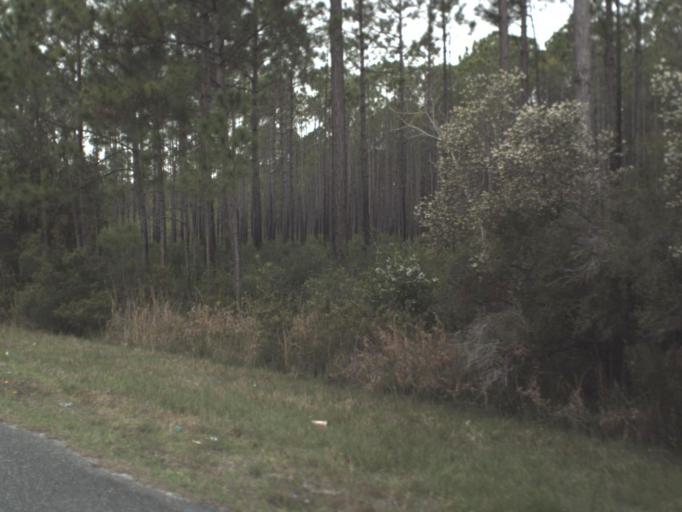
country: US
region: Florida
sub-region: Franklin County
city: Eastpoint
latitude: 29.7888
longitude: -84.8311
